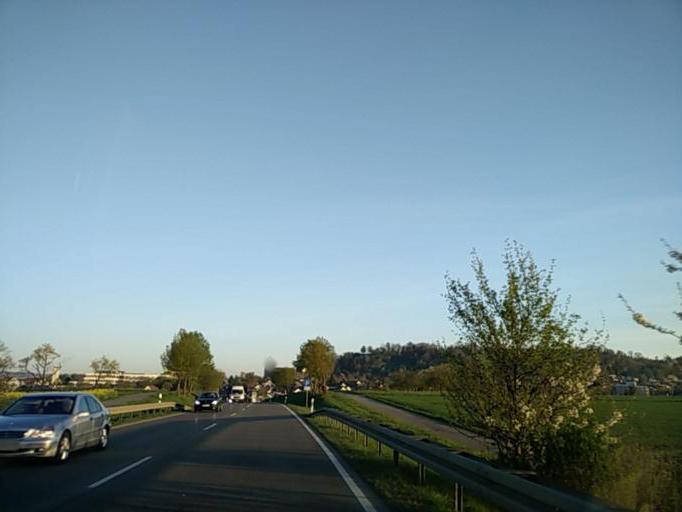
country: DE
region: Baden-Wuerttemberg
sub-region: Regierungsbezirk Stuttgart
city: Herrenberg
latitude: 48.5891
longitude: 8.8815
